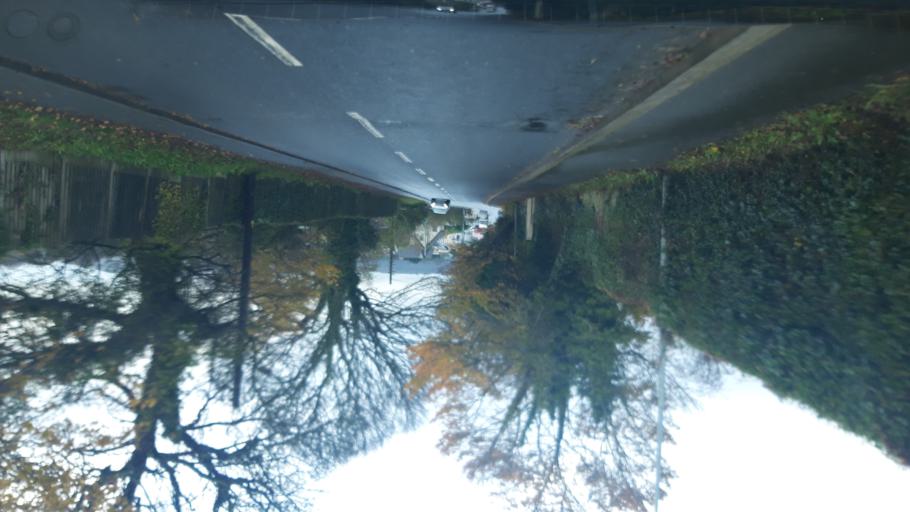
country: IE
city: Newtownmountkennedy
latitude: 53.0876
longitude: -6.1079
